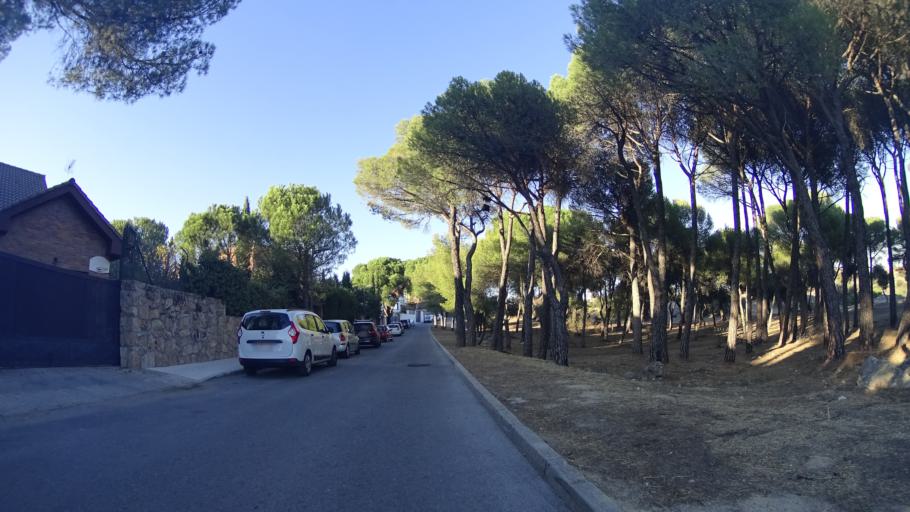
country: ES
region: Madrid
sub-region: Provincia de Madrid
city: Torrelodones
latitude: 40.5711
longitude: -3.9344
